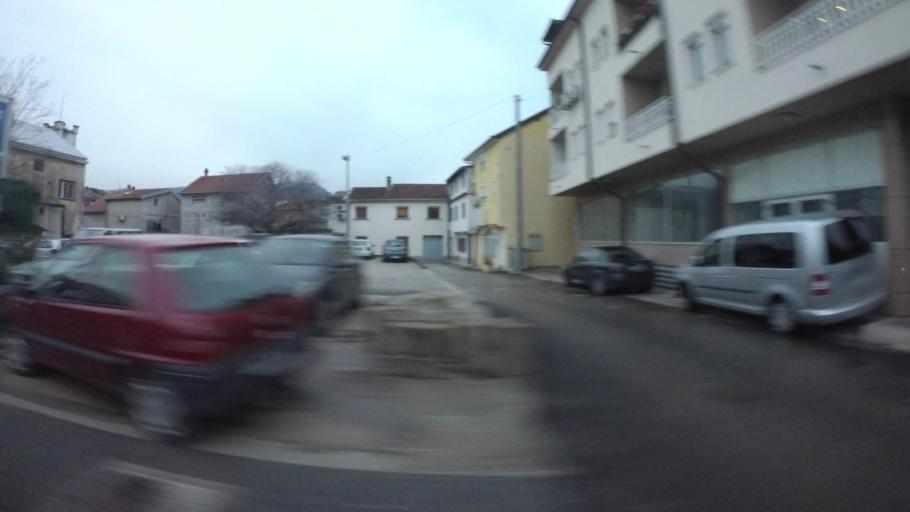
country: BA
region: Federation of Bosnia and Herzegovina
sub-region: Hercegovacko-Bosanski Kanton
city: Mostar
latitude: 43.3452
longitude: 17.8135
